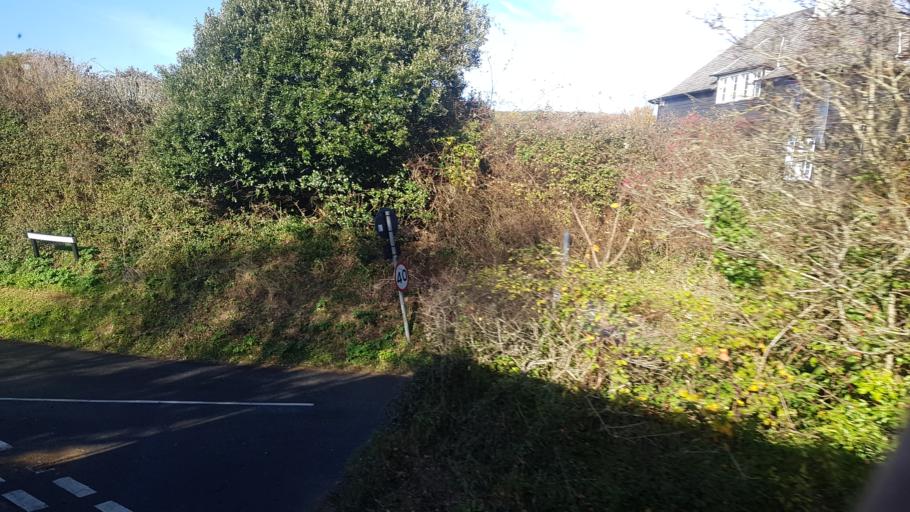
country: GB
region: England
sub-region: Isle of Wight
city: Shalfleet
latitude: 50.6499
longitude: -1.4185
